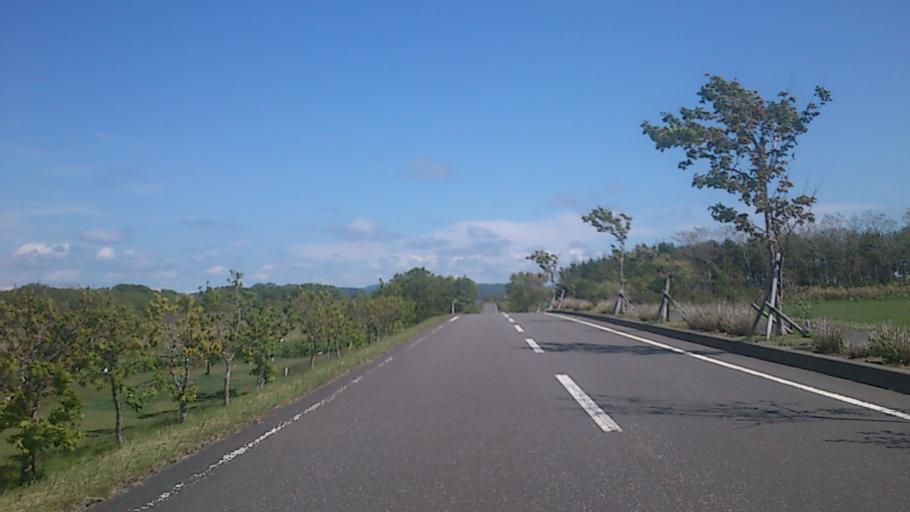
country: JP
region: Hokkaido
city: Rumoi
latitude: 44.5609
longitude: 141.7775
